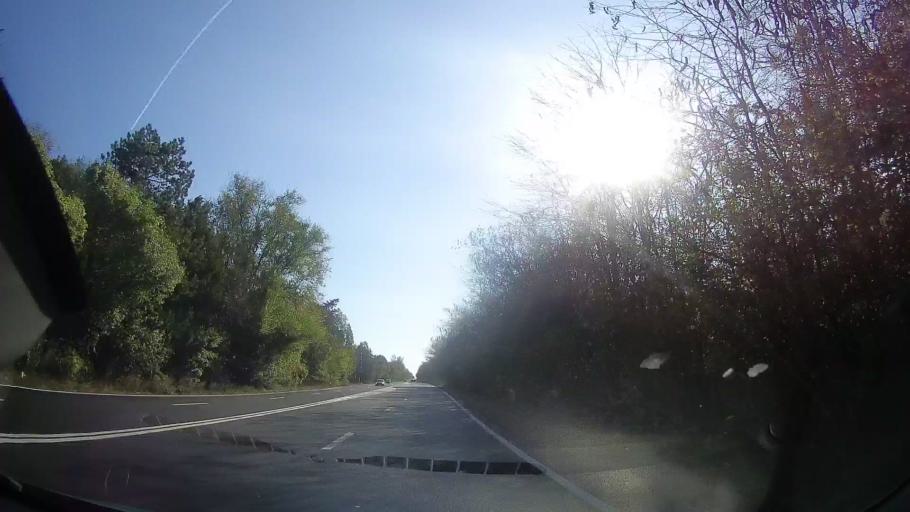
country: RO
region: Constanta
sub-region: Comuna Douazeci si Trei August
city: Dulcesti
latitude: 43.8764
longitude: 28.5739
